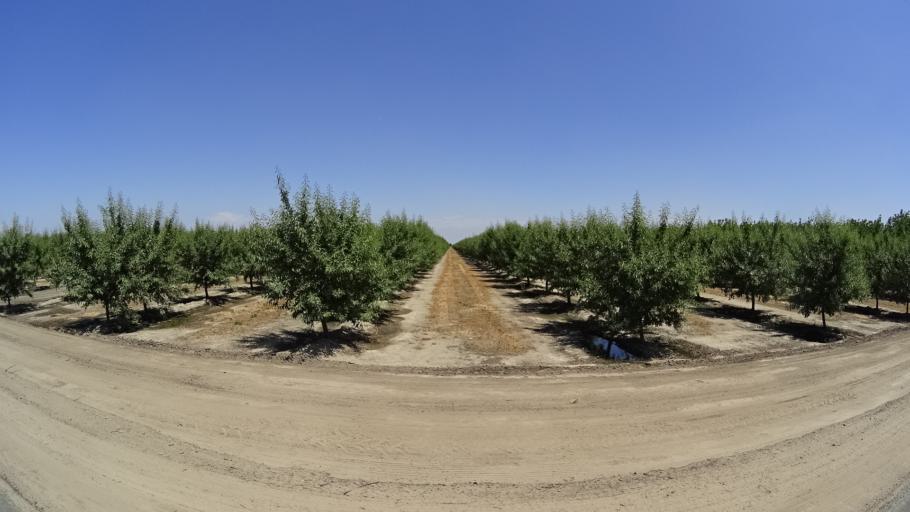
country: US
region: California
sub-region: Kings County
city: Lucerne
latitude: 36.4089
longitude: -119.6549
